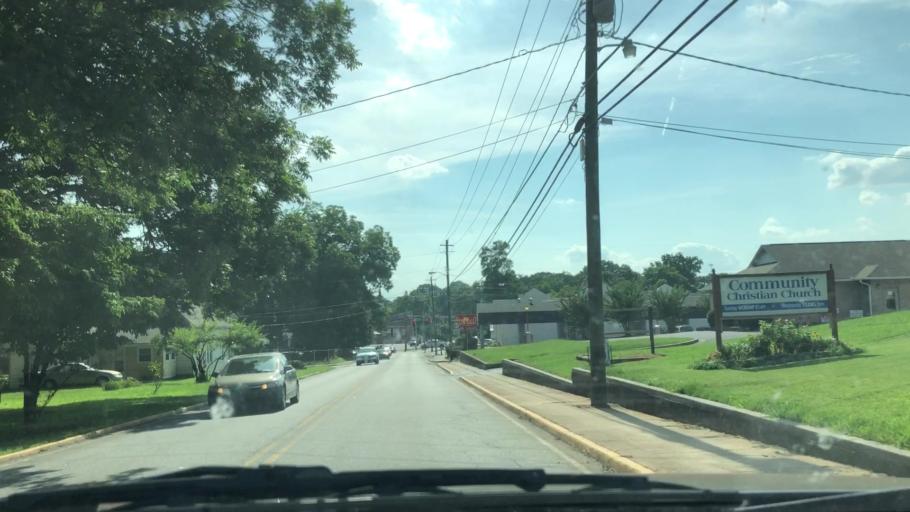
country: US
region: Georgia
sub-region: Bartow County
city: Cartersville
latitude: 34.1761
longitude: -84.7915
